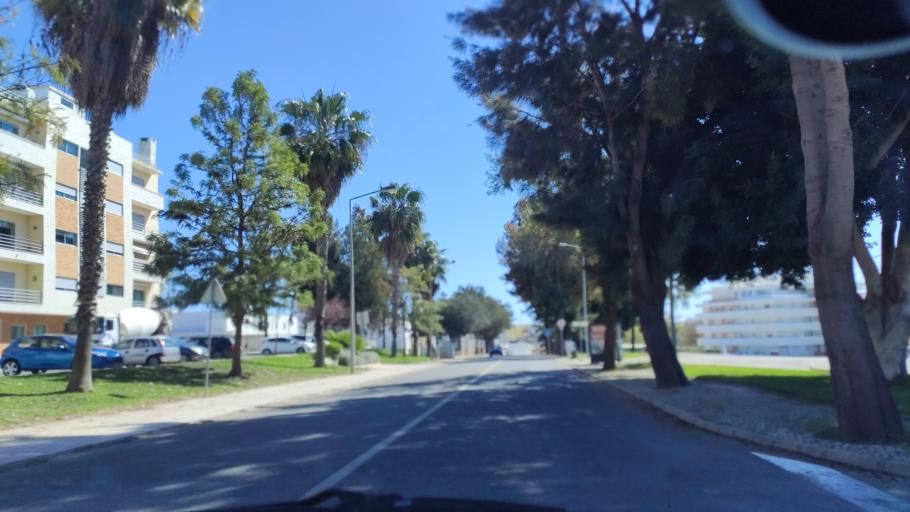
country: PT
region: Faro
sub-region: Olhao
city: Olhao
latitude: 37.0396
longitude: -7.8512
